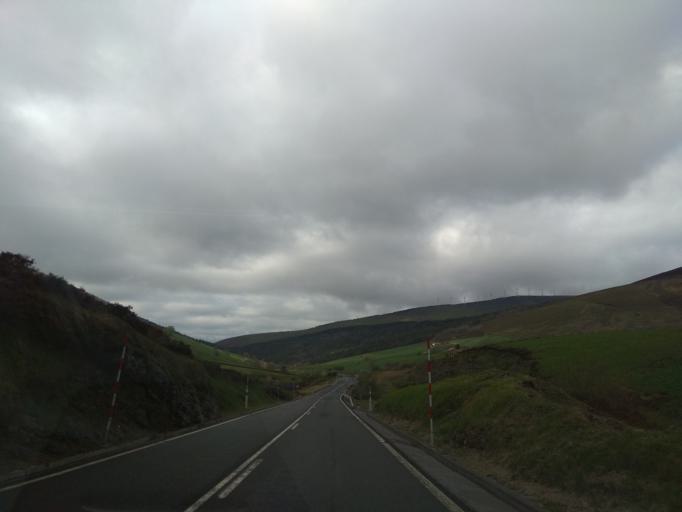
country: ES
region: Basque Country
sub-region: Bizkaia
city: Lanestosa
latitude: 43.1442
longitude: -3.4489
